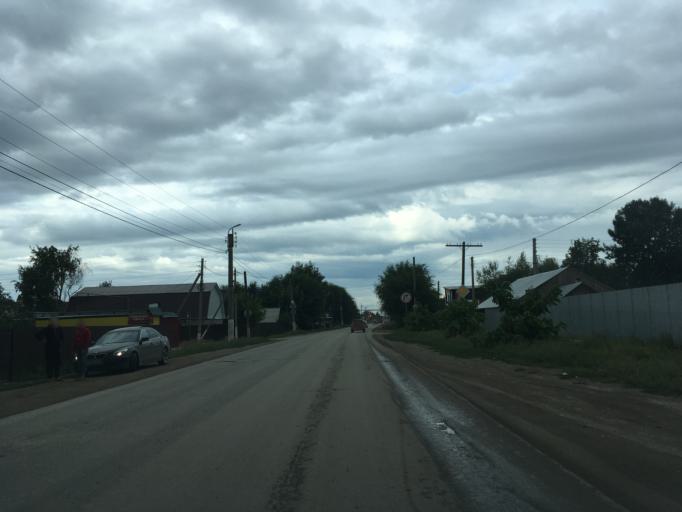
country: RU
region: Samara
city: Bezenchuk
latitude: 52.9814
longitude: 49.4322
